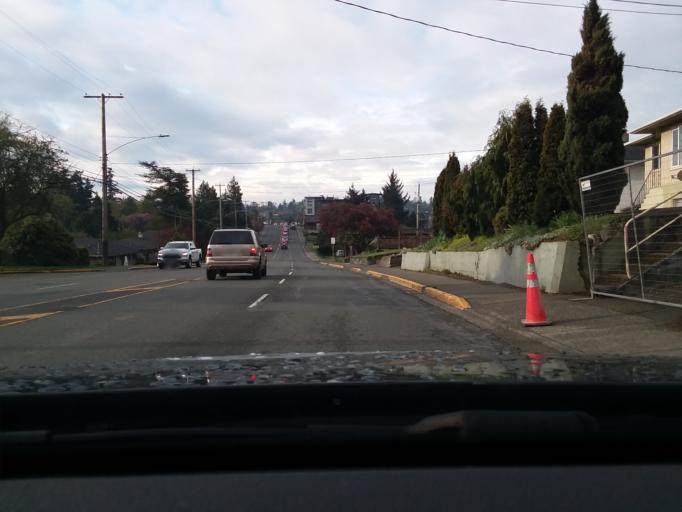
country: CA
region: British Columbia
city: Victoria
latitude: 48.4447
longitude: -123.4014
